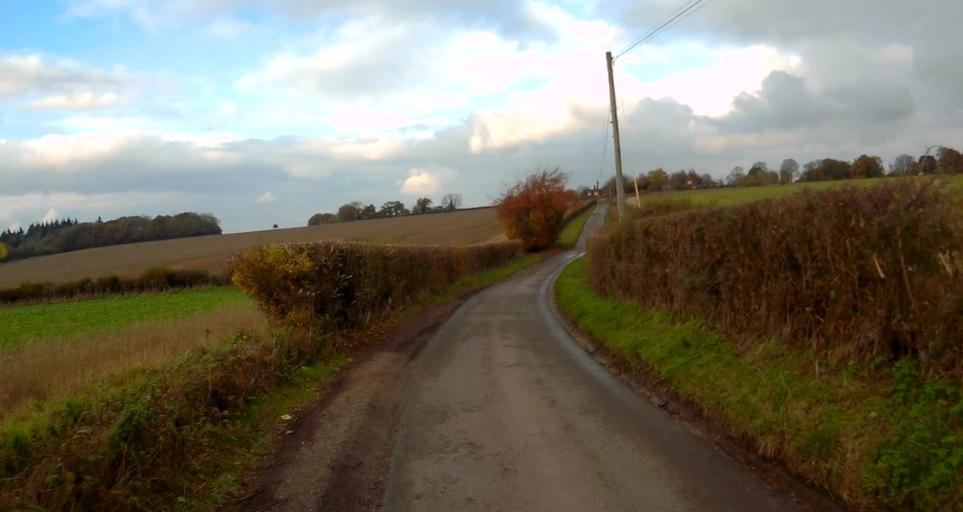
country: GB
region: England
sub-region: Hampshire
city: Long Sutton
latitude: 51.2055
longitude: -0.9420
